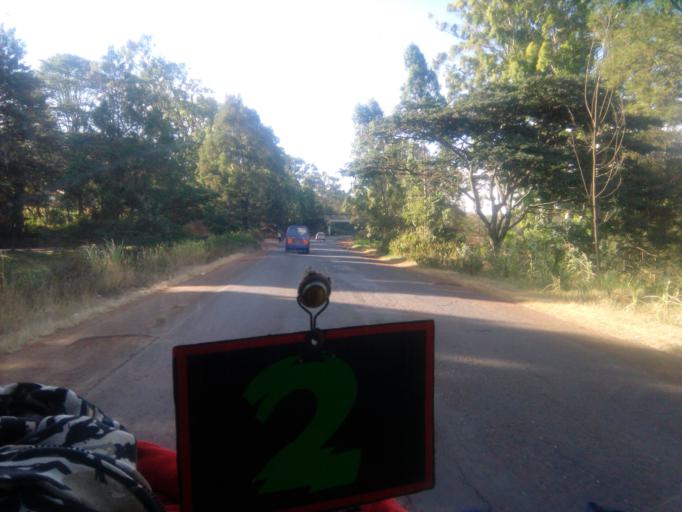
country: KE
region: Kiambu
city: Kikuyu
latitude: -1.2618
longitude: 36.6687
